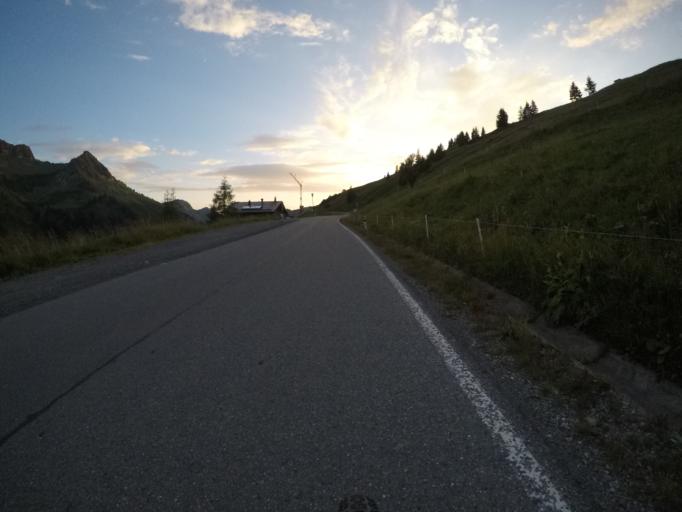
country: AT
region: Vorarlberg
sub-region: Politischer Bezirk Bregenz
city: Damuels
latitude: 47.2818
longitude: 9.8820
